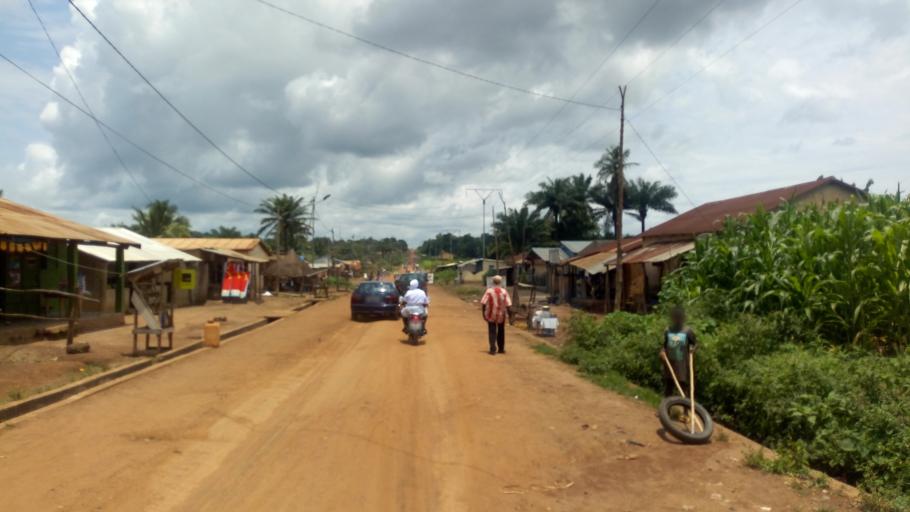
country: TG
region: Centrale
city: Sotouboua
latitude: 8.4335
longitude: 0.9929
